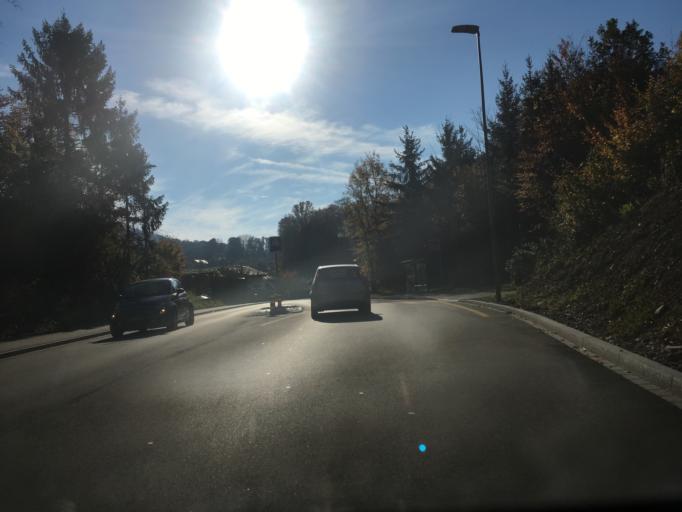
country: CH
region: Zurich
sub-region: Bezirk Dietikon
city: Uitikon
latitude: 47.3606
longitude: 8.4642
